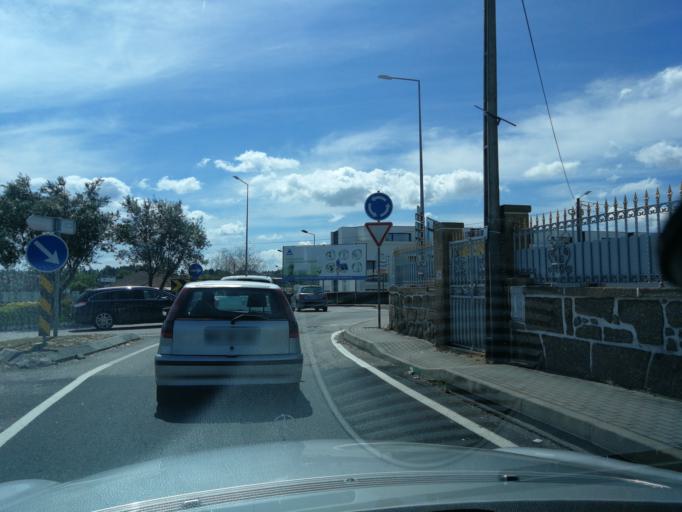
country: PT
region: Braga
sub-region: Vila Nova de Famalicao
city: Calendario
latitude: 41.4167
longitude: -8.5344
